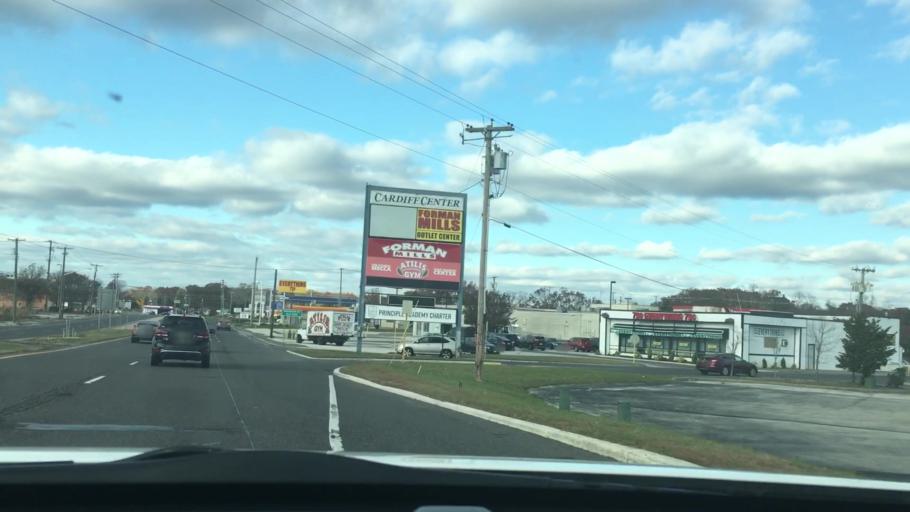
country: US
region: New Jersey
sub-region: Atlantic County
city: Northfield
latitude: 39.4037
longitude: -74.5626
